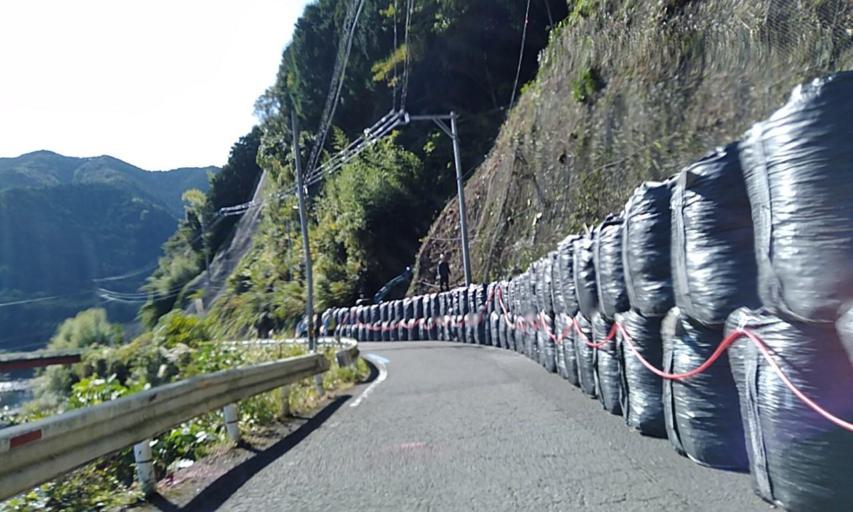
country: JP
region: Wakayama
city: Kainan
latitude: 34.0511
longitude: 135.3141
